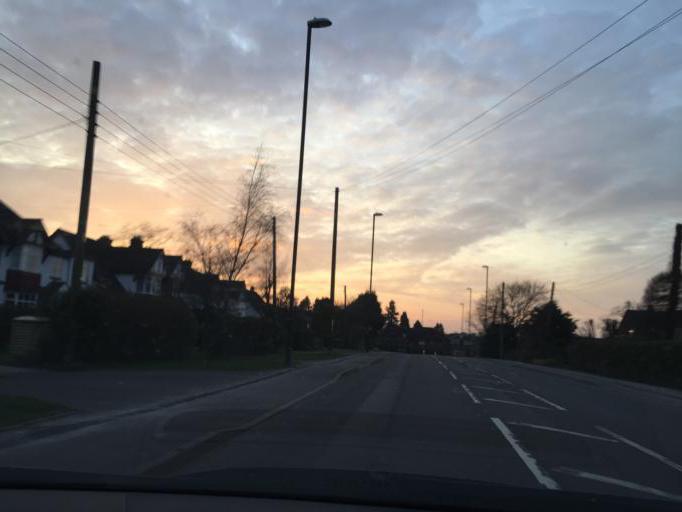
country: GB
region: England
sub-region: Warwickshire
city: Kenilworth
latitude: 52.3888
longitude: -1.5969
